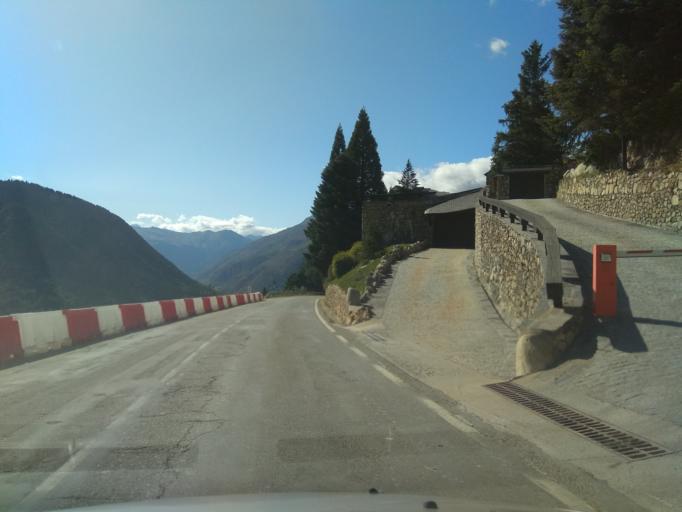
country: ES
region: Catalonia
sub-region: Provincia de Lleida
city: Vielha
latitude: 42.7022
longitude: 0.9305
